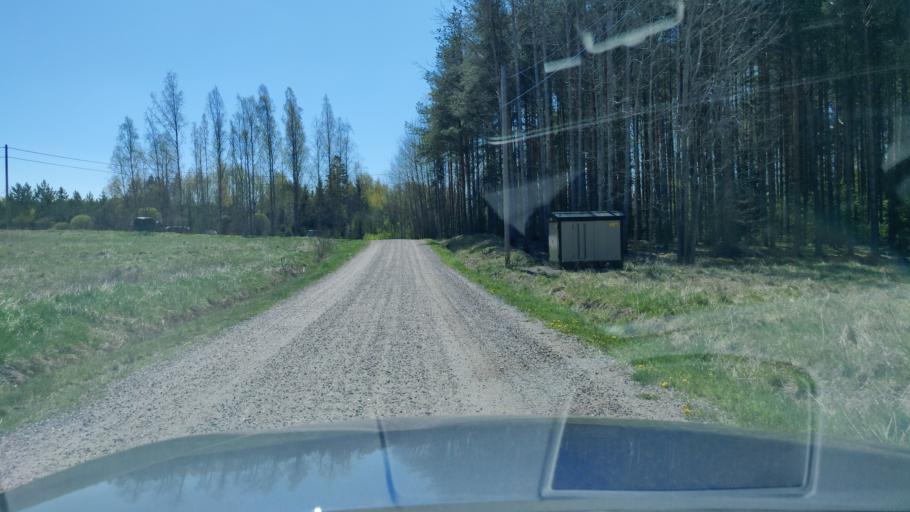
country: FI
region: Uusimaa
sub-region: Helsinki
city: Nurmijaervi
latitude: 60.3567
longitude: 24.7579
